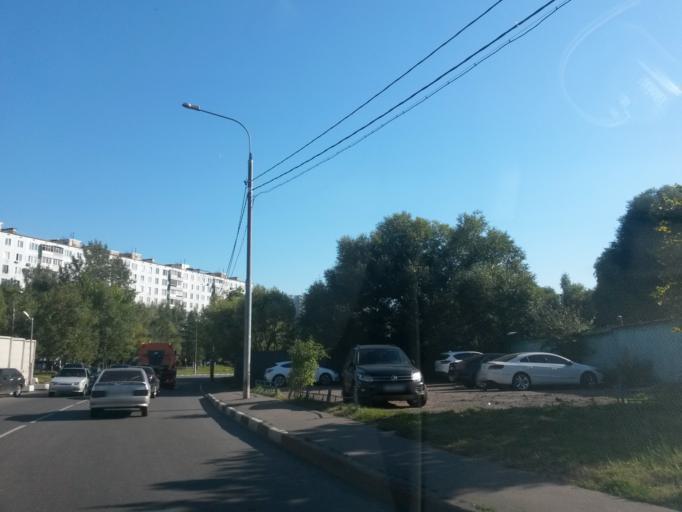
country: RU
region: Moscow
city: Yasenevo
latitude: 55.6098
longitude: 37.5128
